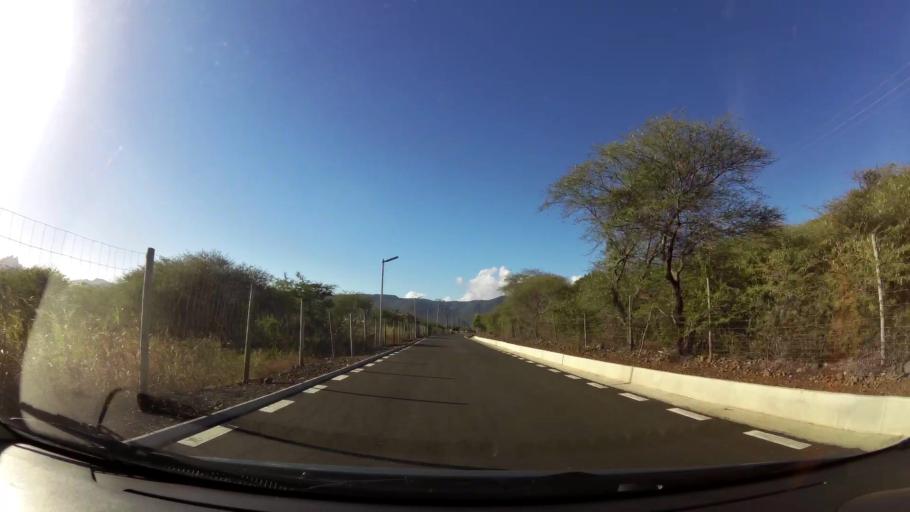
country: MU
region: Black River
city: Tamarin
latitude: -20.3376
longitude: 57.3834
